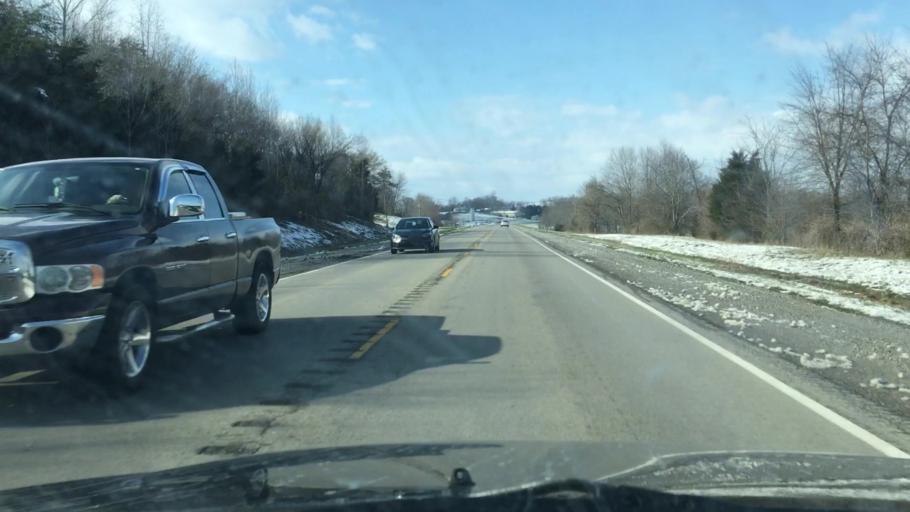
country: US
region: Kentucky
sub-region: Marion County
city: Lebanon
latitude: 37.5300
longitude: -85.3035
